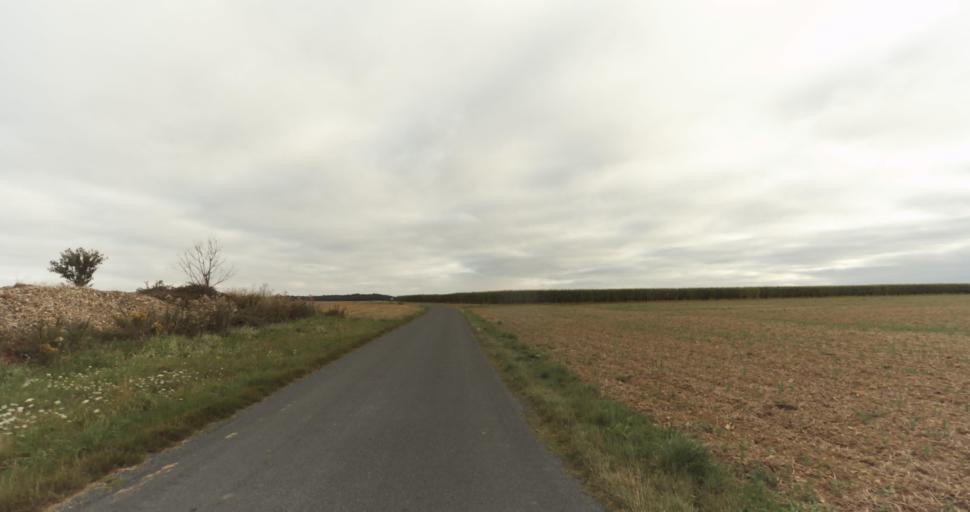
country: FR
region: Haute-Normandie
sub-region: Departement de l'Eure
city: Saint-Germain-sur-Avre
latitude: 48.7832
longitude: 1.2605
